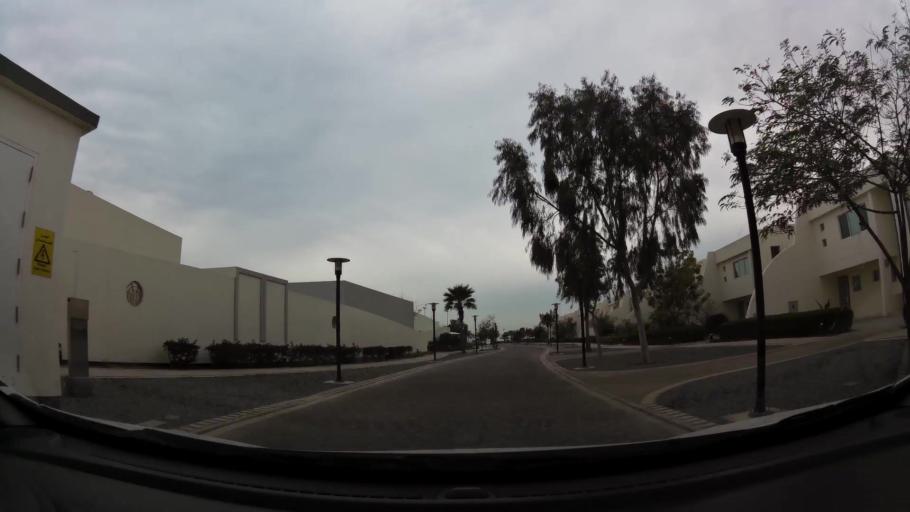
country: BH
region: Central Governorate
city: Dar Kulayb
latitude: 25.8350
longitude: 50.6126
